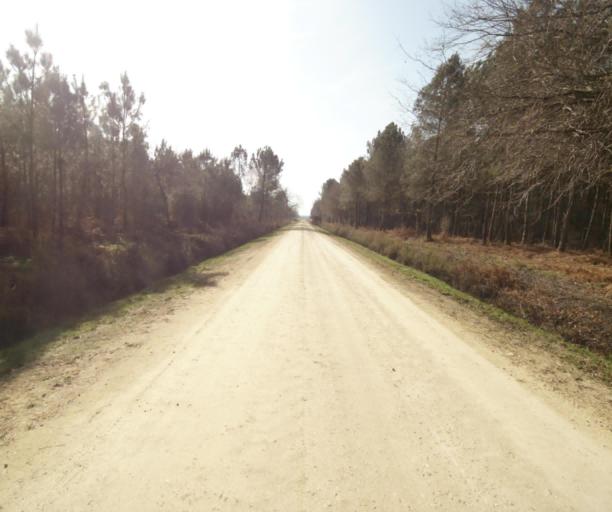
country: FR
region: Aquitaine
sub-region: Departement de la Gironde
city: Grignols
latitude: 44.2162
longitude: -0.1428
